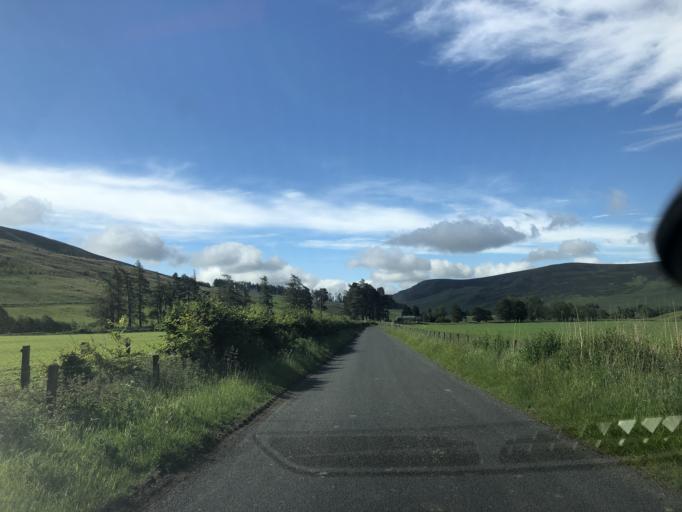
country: GB
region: Scotland
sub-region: Angus
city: Kirriemuir
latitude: 56.8130
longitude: -3.0334
